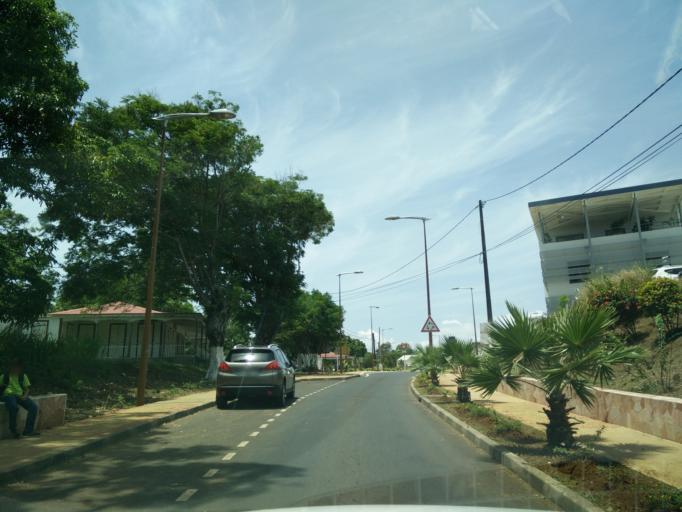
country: GP
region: Guadeloupe
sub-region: Guadeloupe
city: Petit-Bourg
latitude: 16.1941
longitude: -61.5949
